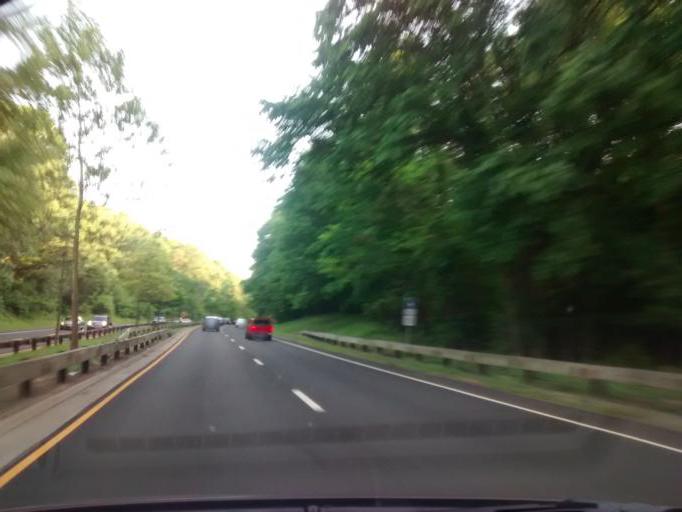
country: US
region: Connecticut
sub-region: Fairfield County
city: Glenville
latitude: 41.0827
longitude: -73.6657
